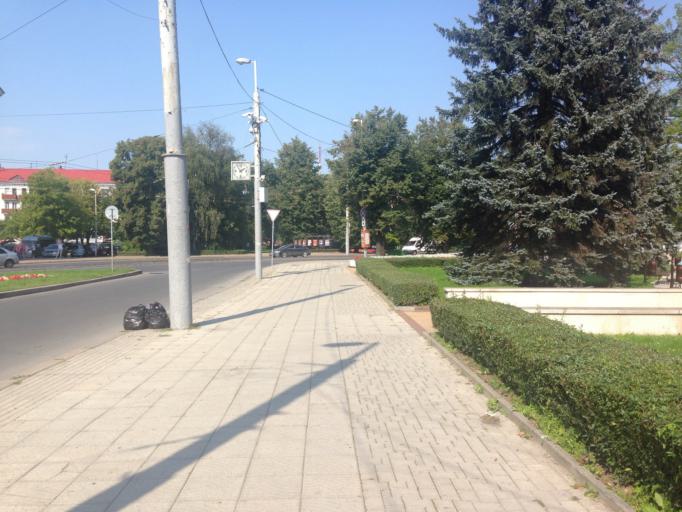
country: RU
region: Kaliningrad
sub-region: Gorod Kaliningrad
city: Kaliningrad
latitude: 54.7191
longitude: 20.4936
